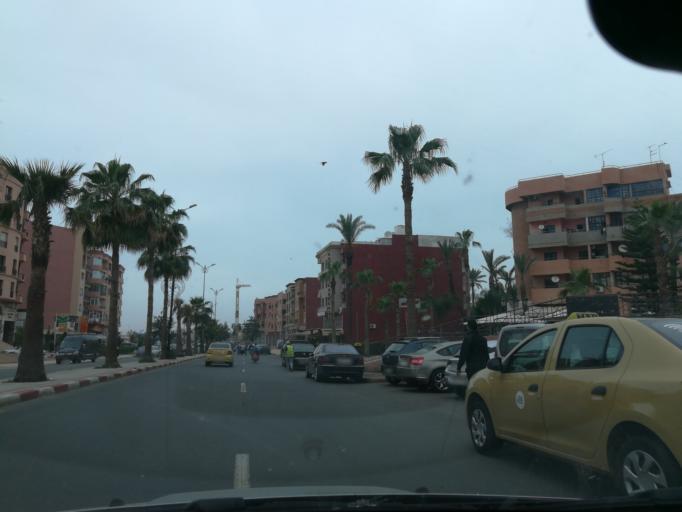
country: MA
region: Marrakech-Tensift-Al Haouz
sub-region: Marrakech
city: Marrakesh
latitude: 31.6651
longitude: -8.0096
